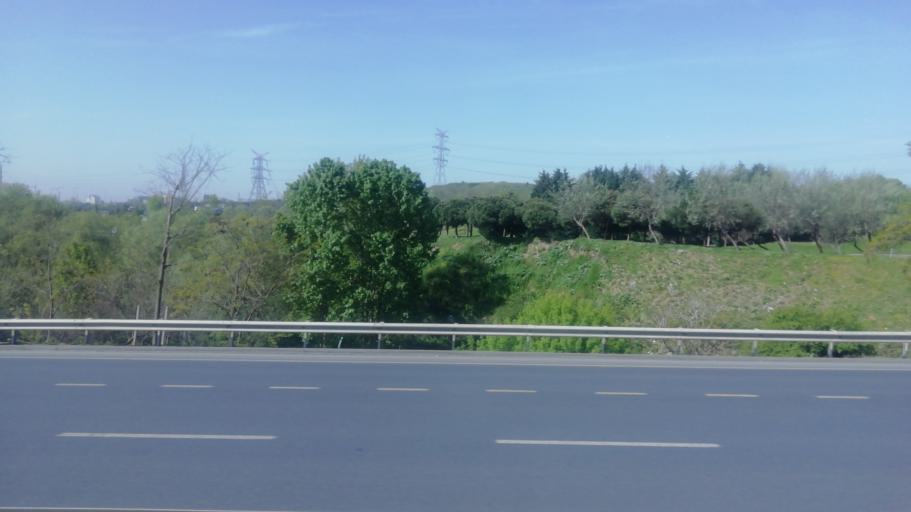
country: TR
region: Istanbul
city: Esenler
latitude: 41.0582
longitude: 28.8885
